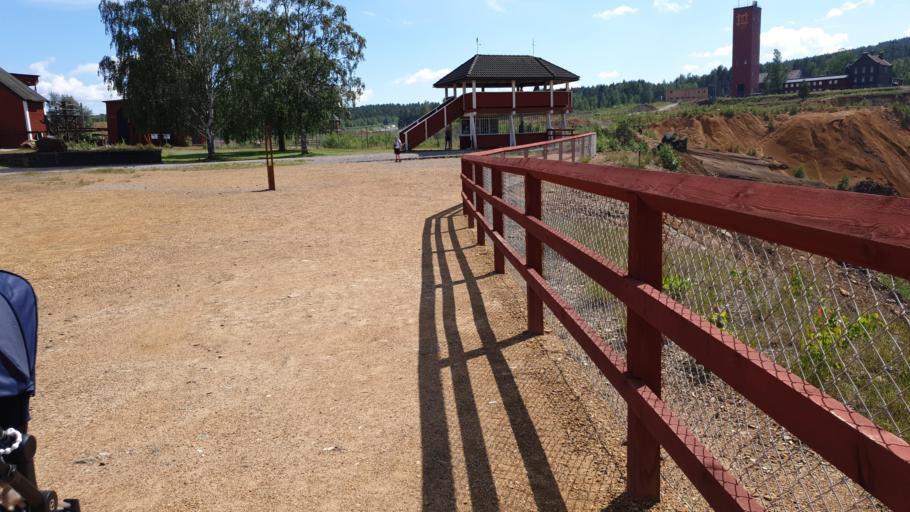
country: SE
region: Dalarna
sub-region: Faluns Kommun
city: Falun
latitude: 60.5999
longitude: 15.6157
